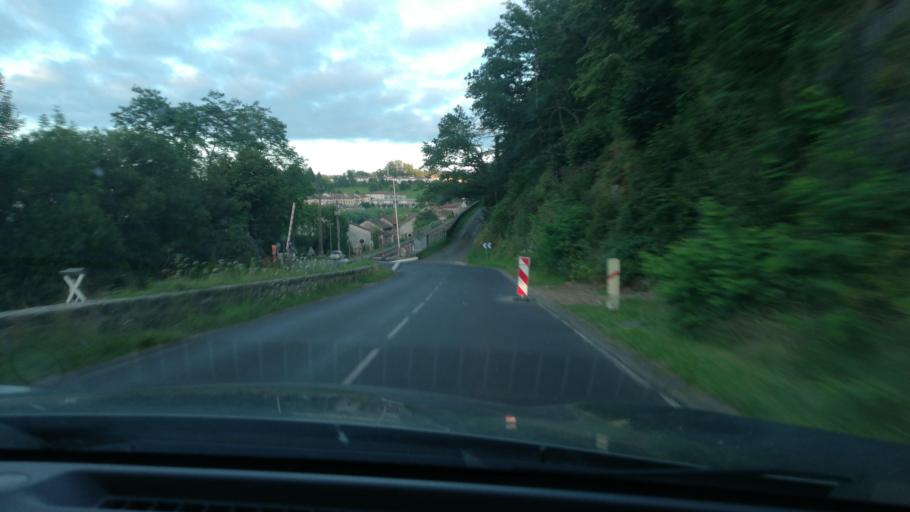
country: FR
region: Auvergne
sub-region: Departement du Cantal
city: Laroquebrou
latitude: 44.9678
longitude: 2.1857
